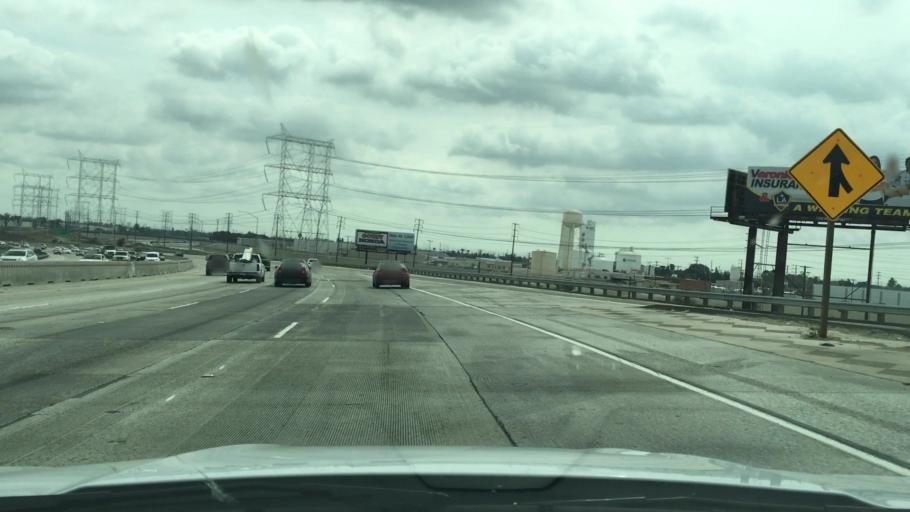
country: US
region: California
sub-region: Los Angeles County
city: Maywood
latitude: 33.9947
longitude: -118.1770
